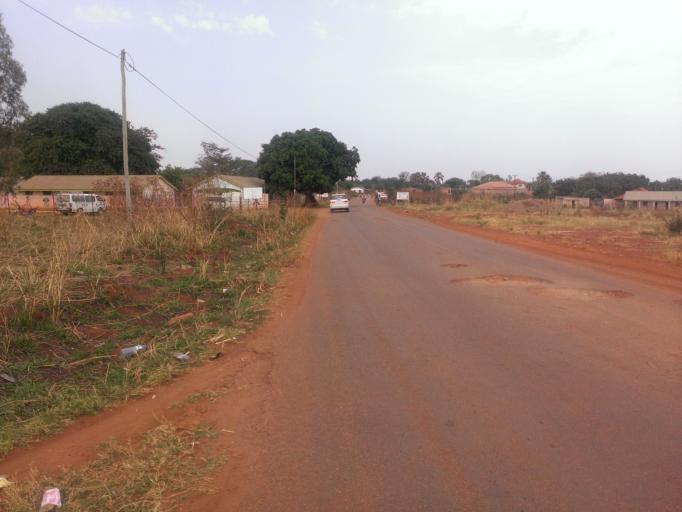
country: UG
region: Northern Region
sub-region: Gulu District
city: Gulu
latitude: 2.7844
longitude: 32.3101
